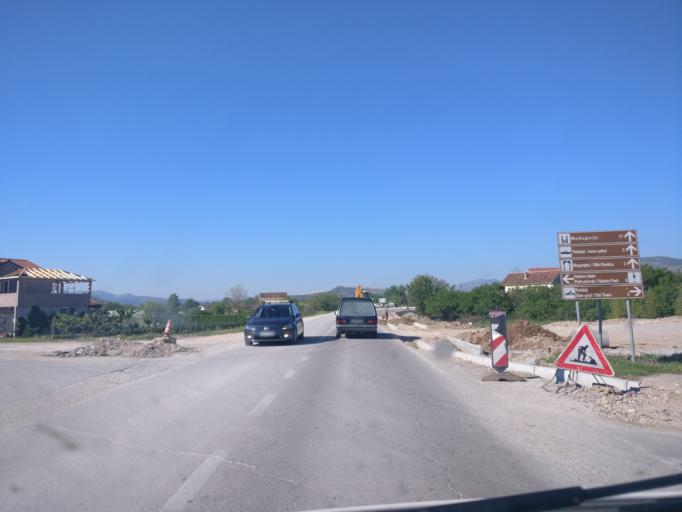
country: BA
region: Federation of Bosnia and Herzegovina
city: Tasovcici
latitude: 43.1089
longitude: 17.7205
